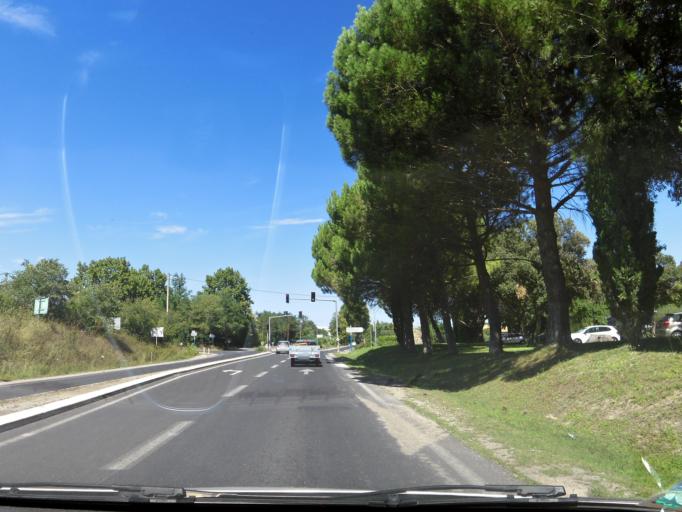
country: FR
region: Languedoc-Roussillon
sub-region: Departement de l'Herault
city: Vendargues
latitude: 43.6597
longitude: 3.9645
